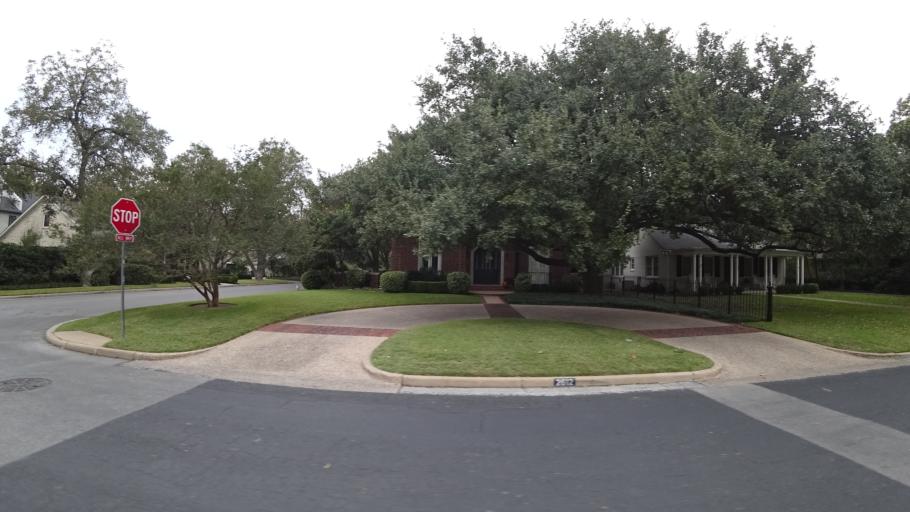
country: US
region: Texas
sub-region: Travis County
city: Austin
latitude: 30.2964
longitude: -97.7545
